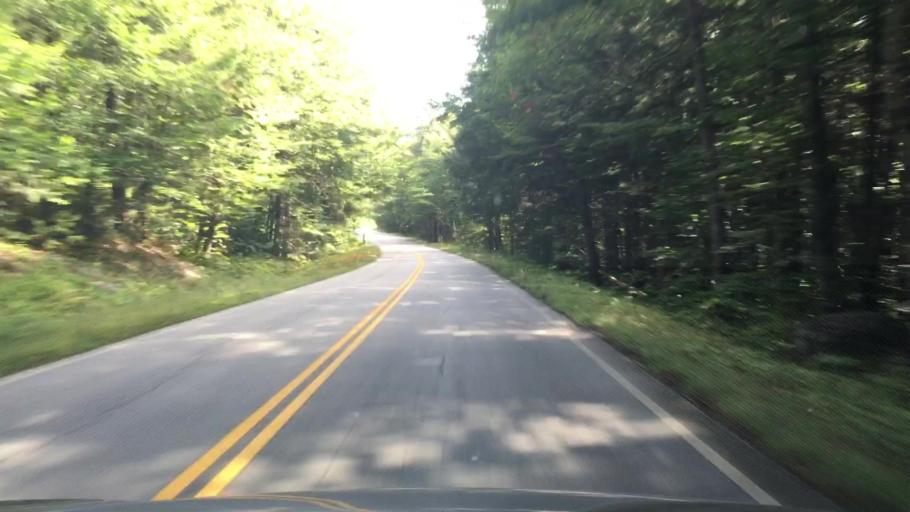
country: US
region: New Hampshire
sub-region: Carroll County
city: Tamworth
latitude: 44.0083
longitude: -71.3211
